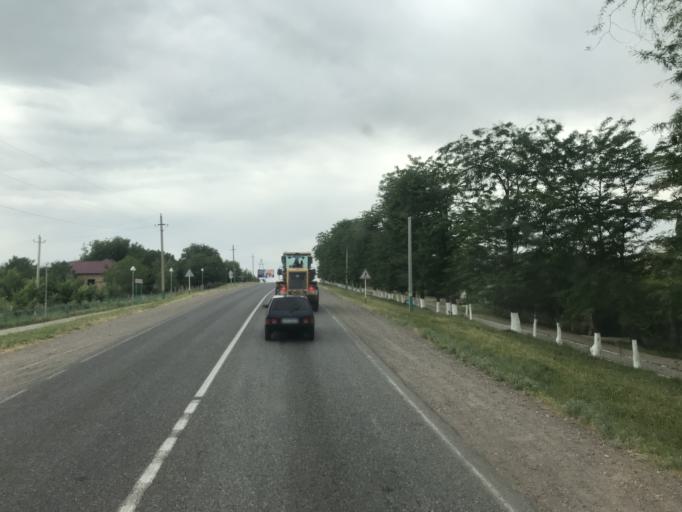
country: UZ
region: Toshkent
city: Salor
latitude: 41.4942
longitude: 69.3244
